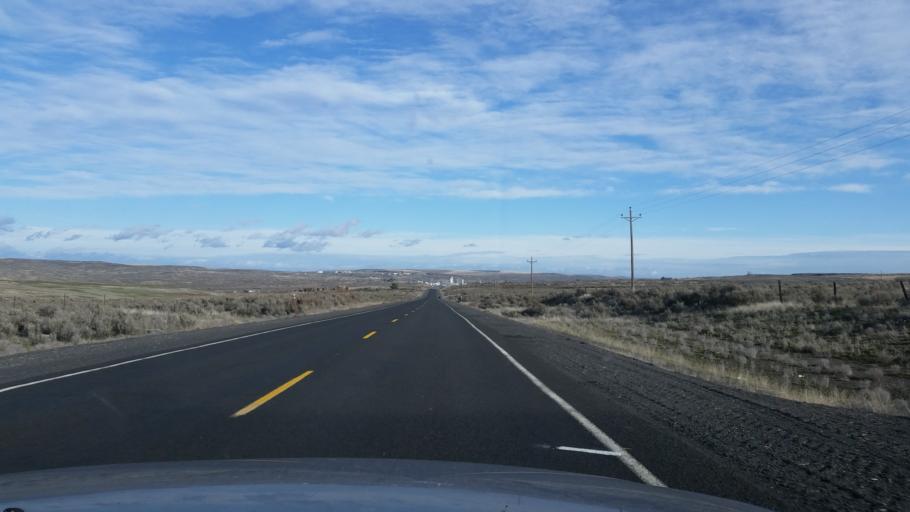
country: US
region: Washington
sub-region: Adams County
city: Ritzville
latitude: 47.3212
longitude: -118.7319
